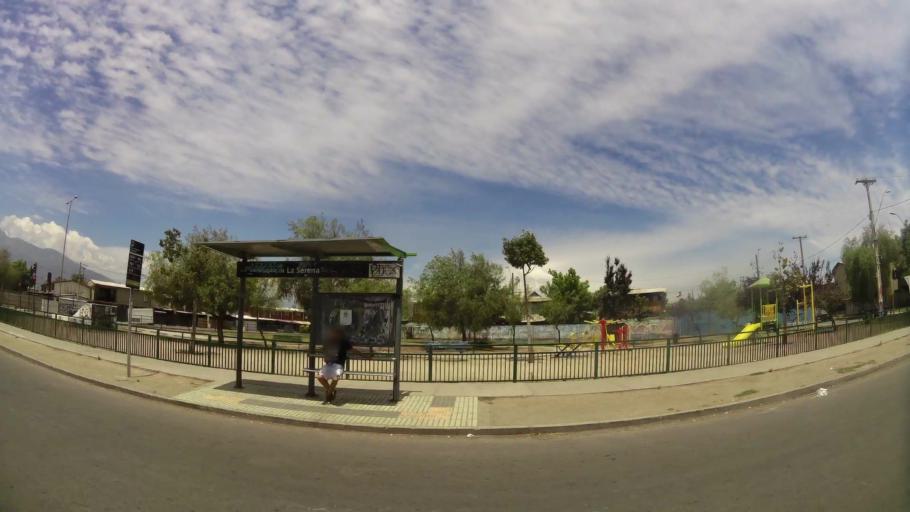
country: CL
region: Santiago Metropolitan
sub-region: Provincia de Santiago
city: La Pintana
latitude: -33.5609
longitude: -70.6156
